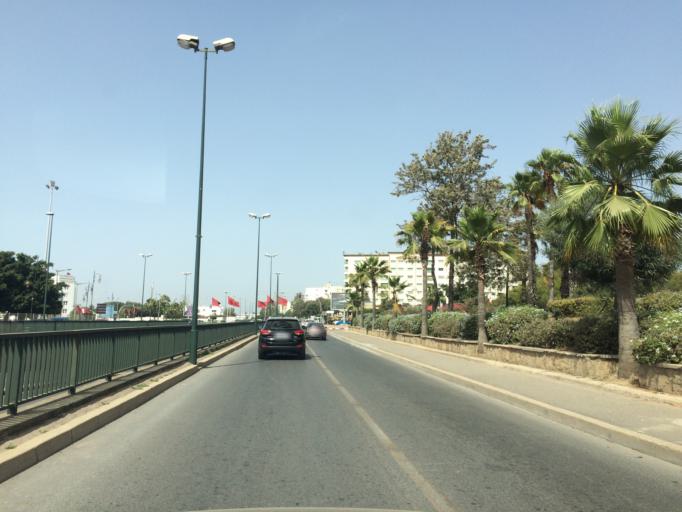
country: MA
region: Rabat-Sale-Zemmour-Zaer
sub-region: Rabat
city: Rabat
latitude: 33.9856
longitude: -6.8527
